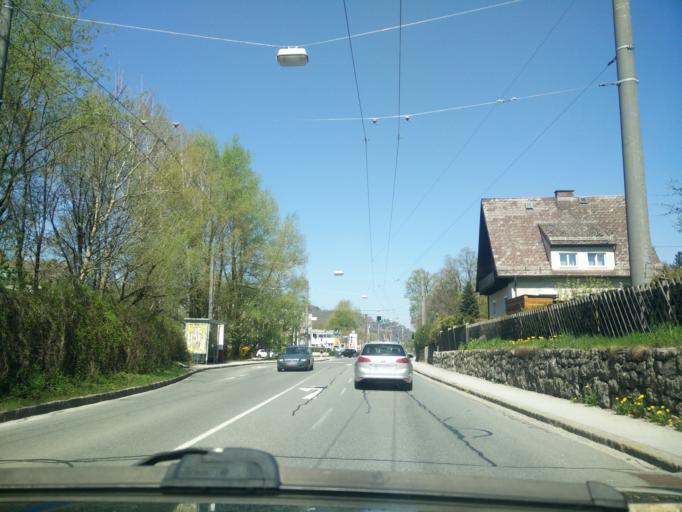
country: AT
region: Salzburg
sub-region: Politischer Bezirk Salzburg-Umgebung
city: Elsbethen
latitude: 47.7825
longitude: 13.0815
